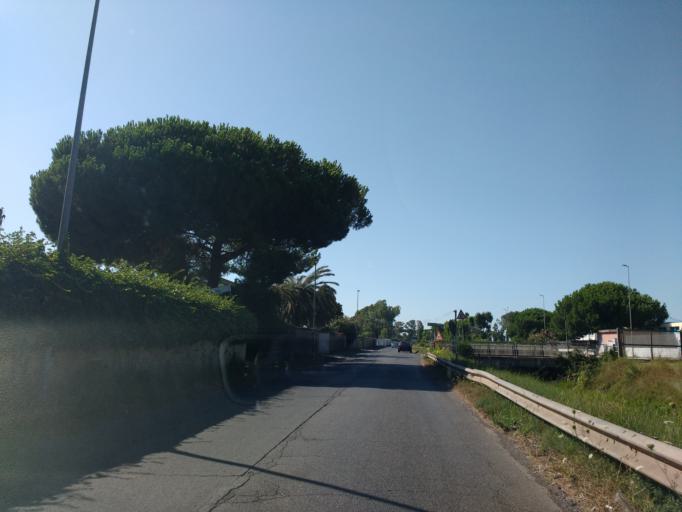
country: IT
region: Latium
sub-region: Citta metropolitana di Roma Capitale
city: Acilia-Castel Fusano-Ostia Antica
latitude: 41.7471
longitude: 12.3337
